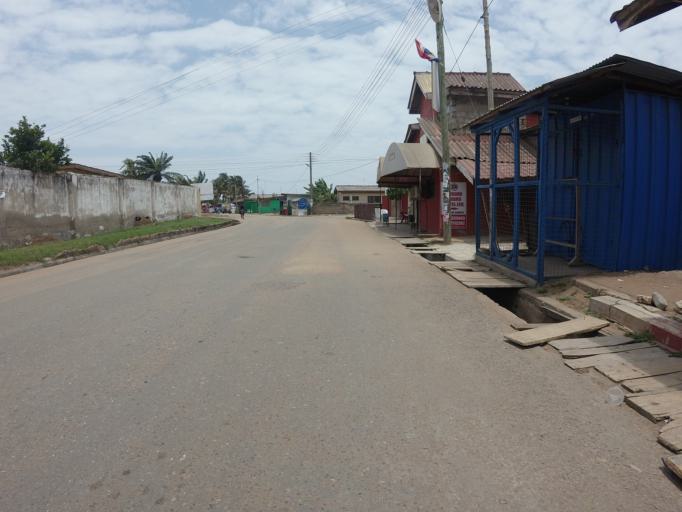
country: GH
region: Greater Accra
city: Nungua
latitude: 5.6018
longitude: -0.0846
